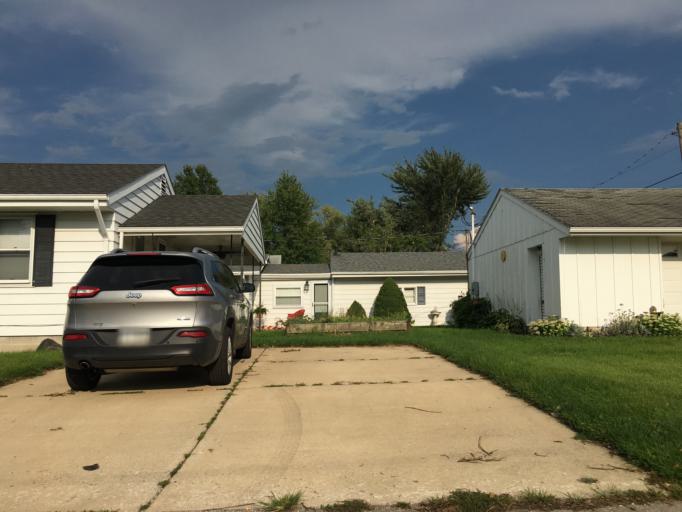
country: US
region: Indiana
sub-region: Howard County
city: Kokomo
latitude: 40.4668
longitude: -86.1176
